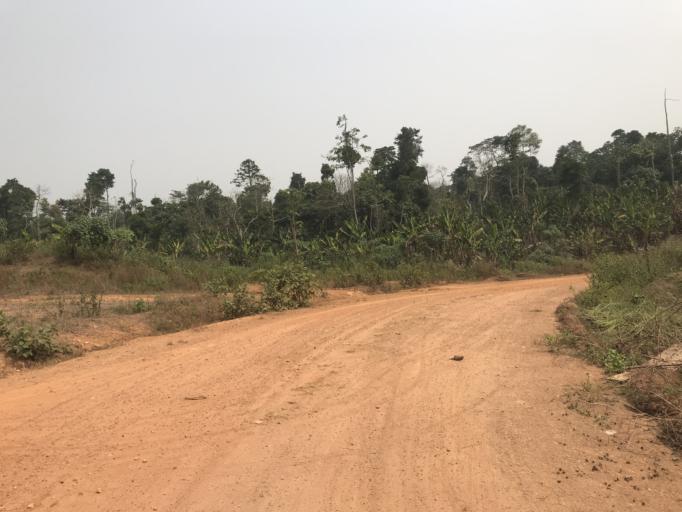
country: NG
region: Osun
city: Ifetedo
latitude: 7.0520
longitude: 4.4736
